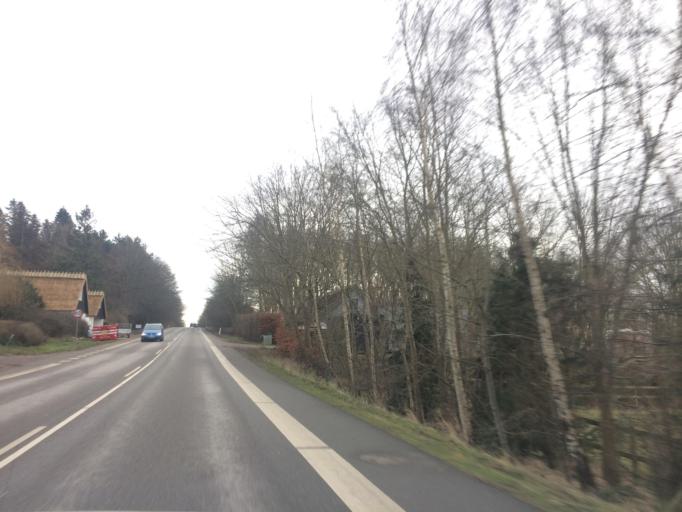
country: DK
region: Capital Region
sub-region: Fredensborg Kommune
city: Fredensborg
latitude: 55.9415
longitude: 12.4287
